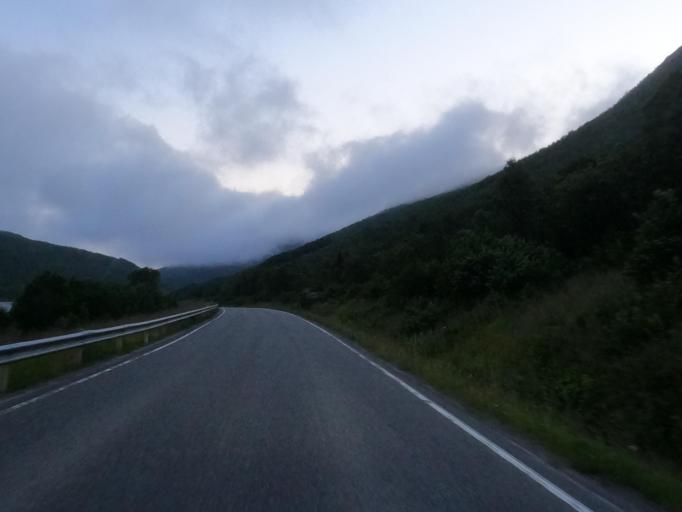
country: NO
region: Nordland
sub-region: Sortland
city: Sortland
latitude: 68.6199
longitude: 15.7103
